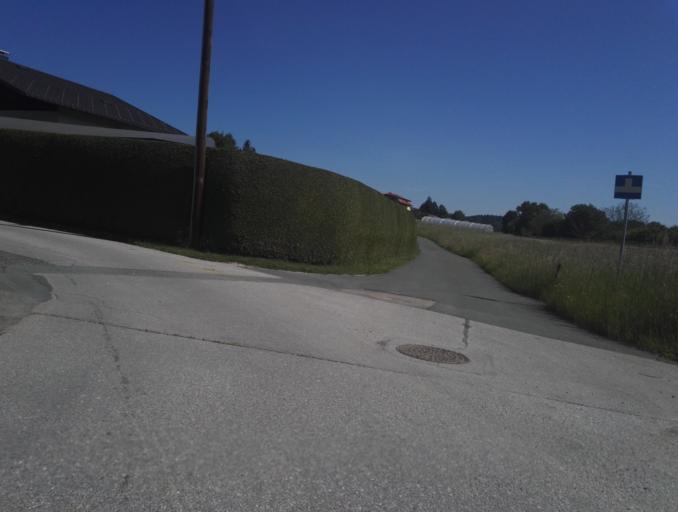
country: AT
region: Styria
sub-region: Politischer Bezirk Graz-Umgebung
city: Raaba
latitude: 47.0360
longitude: 15.5030
